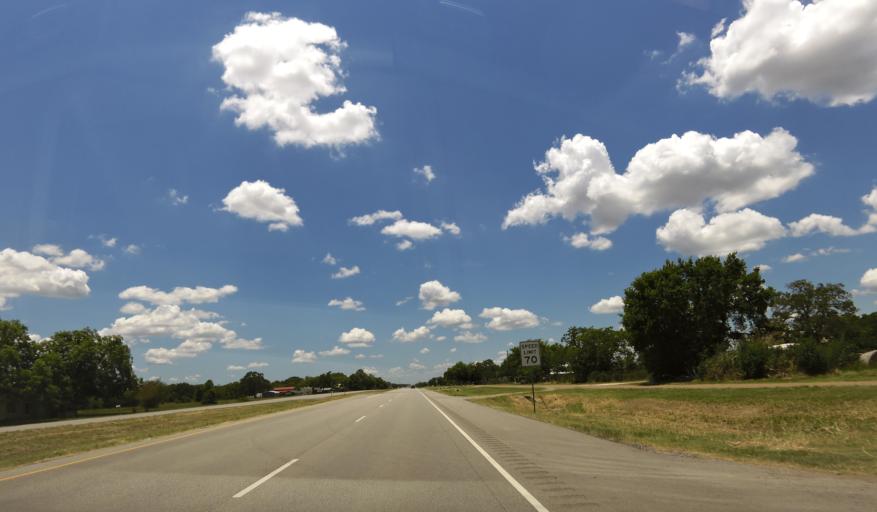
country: US
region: Texas
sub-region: Burleson County
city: Somerville
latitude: 30.1505
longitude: -96.6798
